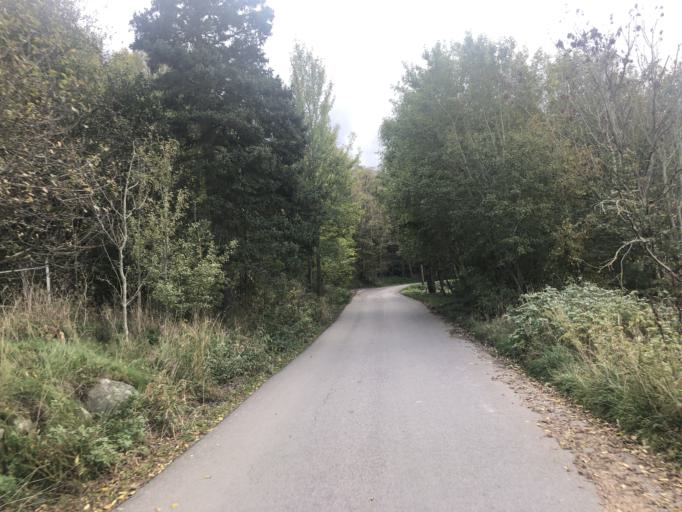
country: SE
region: Vaestra Goetaland
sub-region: Molndal
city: Moelndal
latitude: 57.6411
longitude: 11.9791
